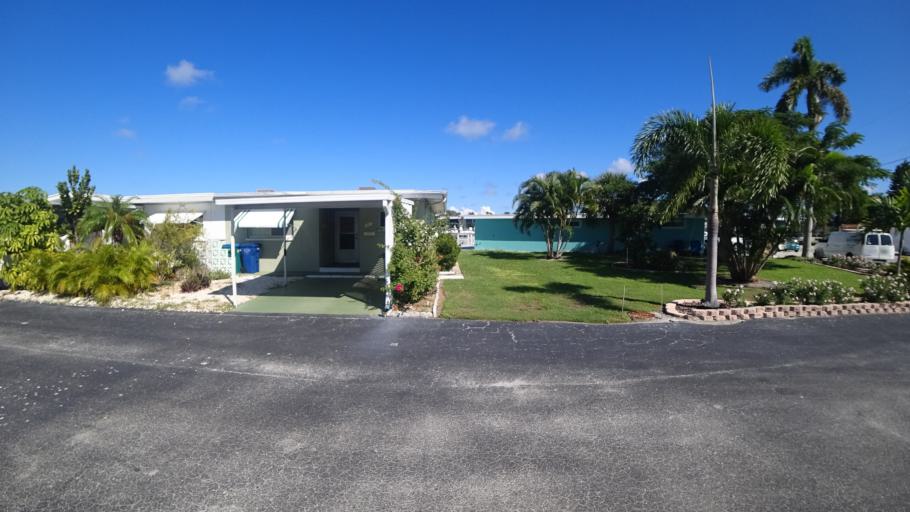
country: US
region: Florida
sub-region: Manatee County
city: Holmes Beach
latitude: 27.5135
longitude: -82.7153
